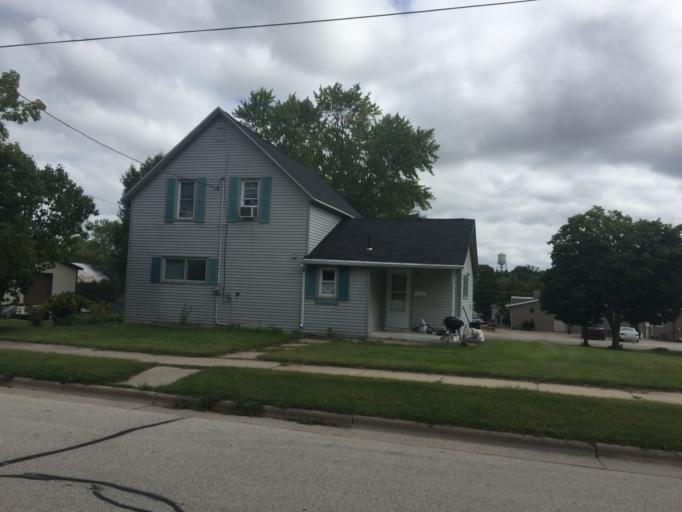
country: US
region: Wisconsin
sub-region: Oconto County
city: Oconto Falls
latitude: 44.8724
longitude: -88.1478
